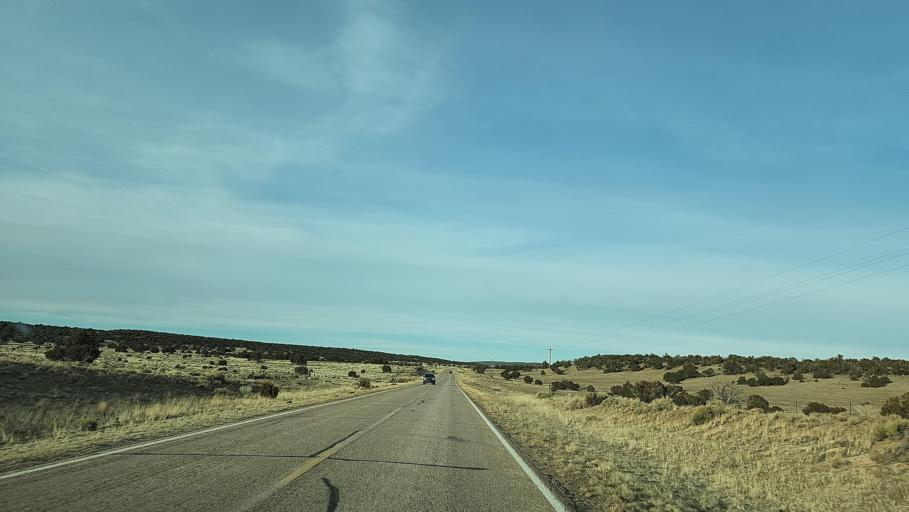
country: US
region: New Mexico
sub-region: Catron County
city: Reserve
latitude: 34.3922
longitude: -108.4474
